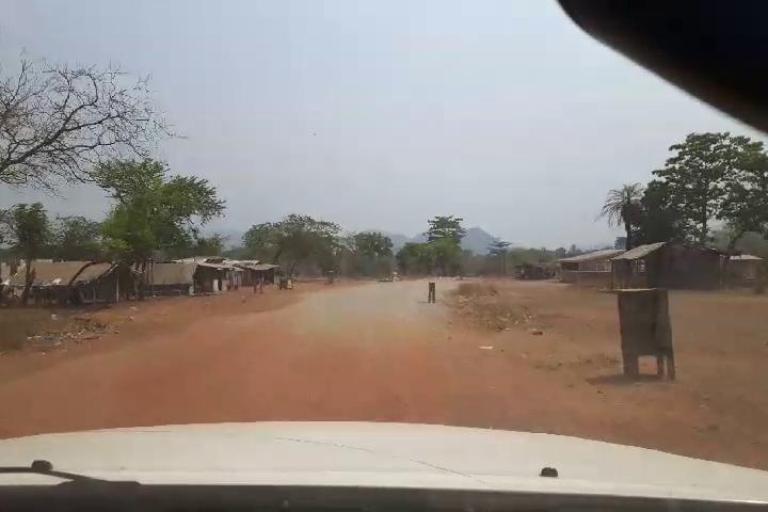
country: SL
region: Northern Province
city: Bumbuna
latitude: 9.0033
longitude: -11.7779
